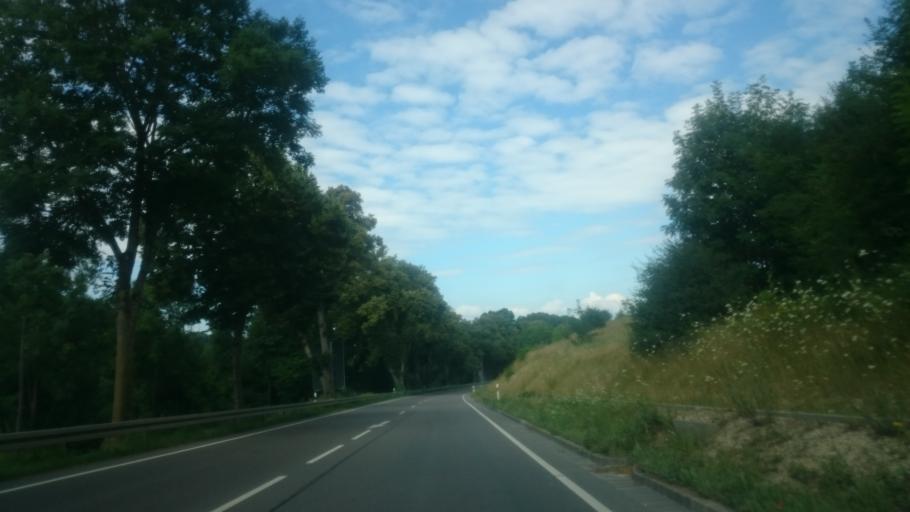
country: DE
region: Bavaria
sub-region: Regierungsbezirk Mittelfranken
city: Weissenburg in Bayern
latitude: 49.0191
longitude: 11.0018
